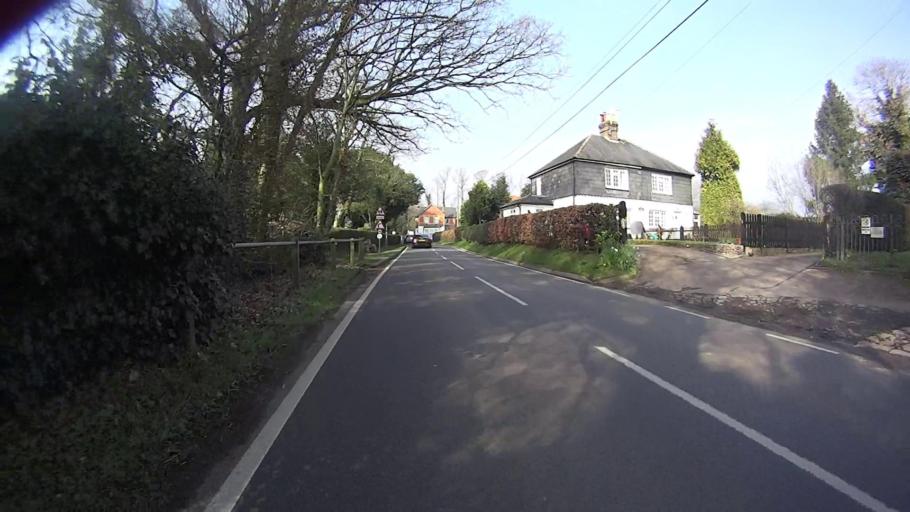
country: GB
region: England
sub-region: West Sussex
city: Copthorne
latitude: 51.1822
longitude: -0.0881
